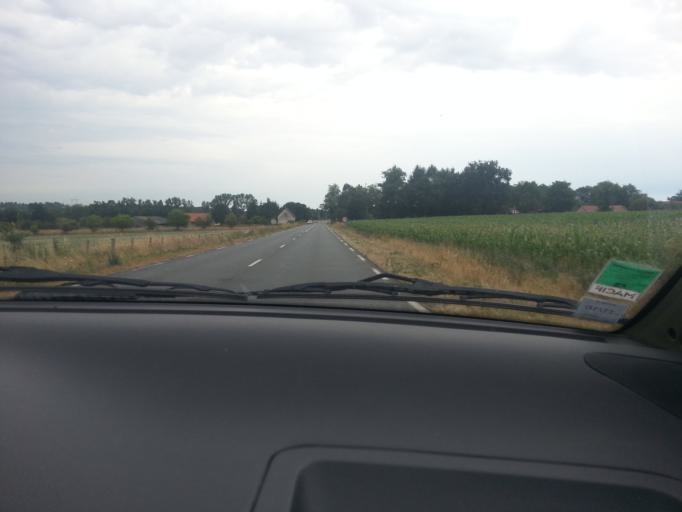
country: FR
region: Auvergne
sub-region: Departement de l'Allier
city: Saint-Gerand-le-Puy
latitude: 46.2026
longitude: 3.4983
